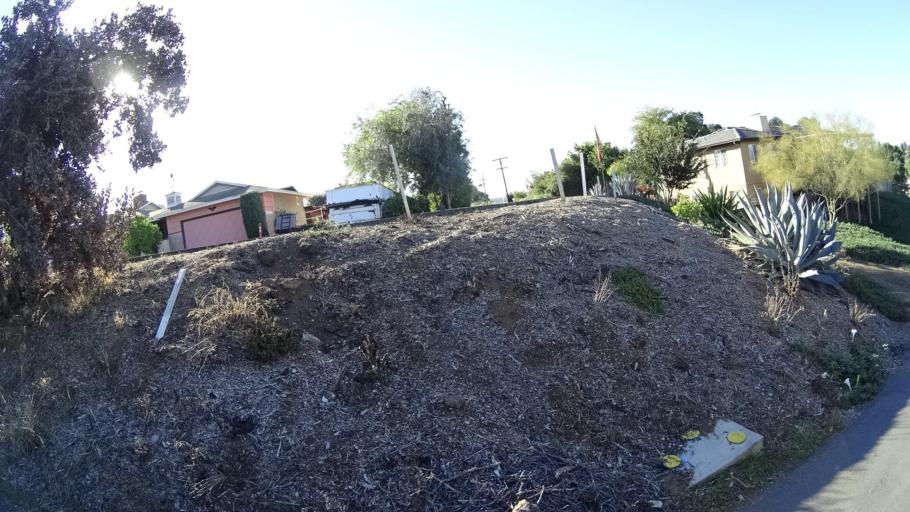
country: US
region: California
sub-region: San Diego County
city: Bonita
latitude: 32.6803
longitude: -117.0227
